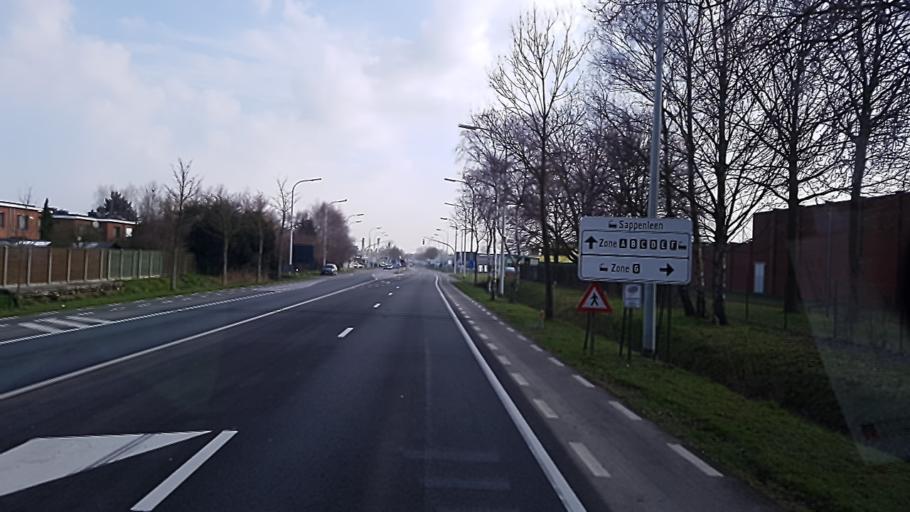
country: BE
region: Flanders
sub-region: Provincie West-Vlaanderen
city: Poperinge
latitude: 50.8471
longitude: 2.7369
